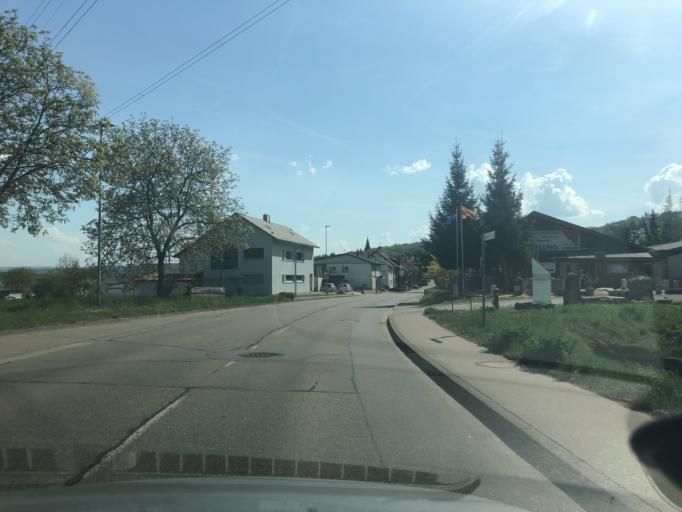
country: DE
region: Baden-Wuerttemberg
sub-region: Freiburg Region
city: Weilheim
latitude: 47.6451
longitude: 8.2470
